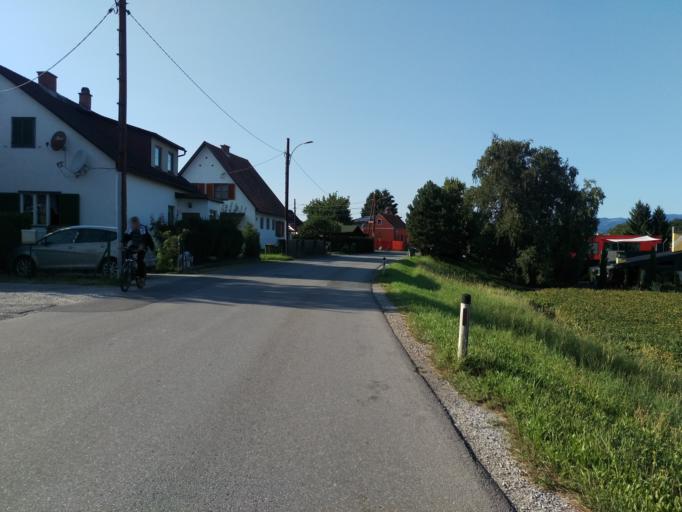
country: AT
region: Styria
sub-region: Politischer Bezirk Graz-Umgebung
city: Feldkirchen bei Graz
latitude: 47.0241
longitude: 15.4417
